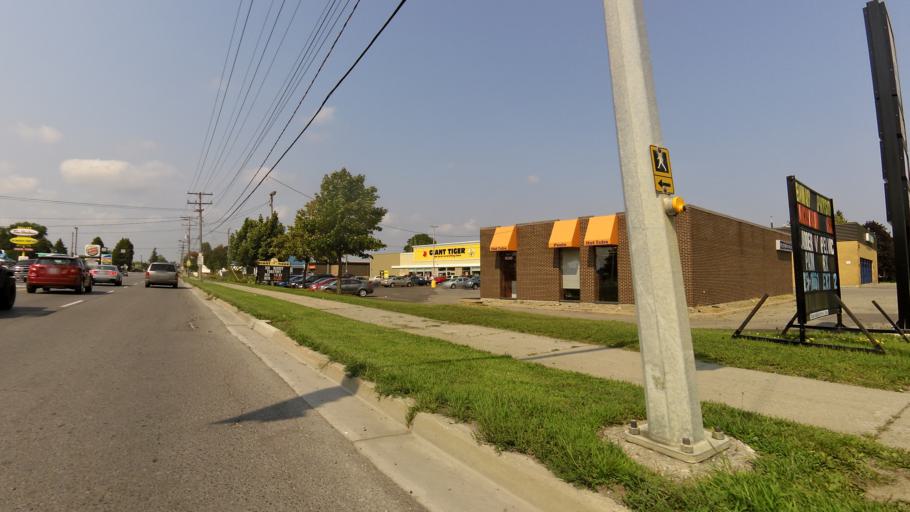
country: CA
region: Ontario
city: Prescott
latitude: 44.7168
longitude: -75.5200
